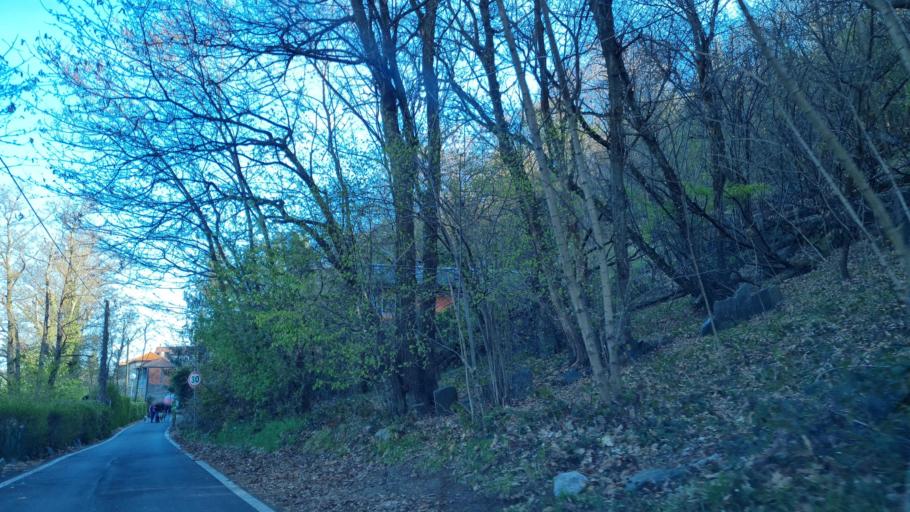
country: IT
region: Piedmont
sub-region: Provincia di Novara
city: San Maurizio D'Opaglio
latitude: 45.7771
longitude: 8.4079
